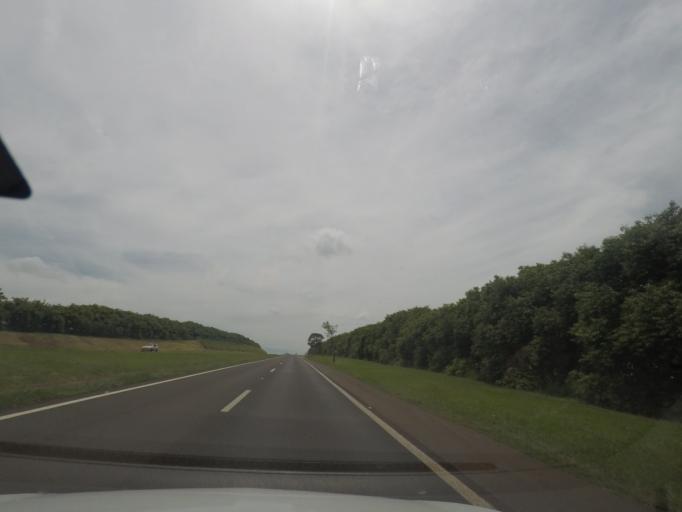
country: BR
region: Sao Paulo
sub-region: Bebedouro
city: Bebedouro
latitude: -21.0146
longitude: -48.4259
